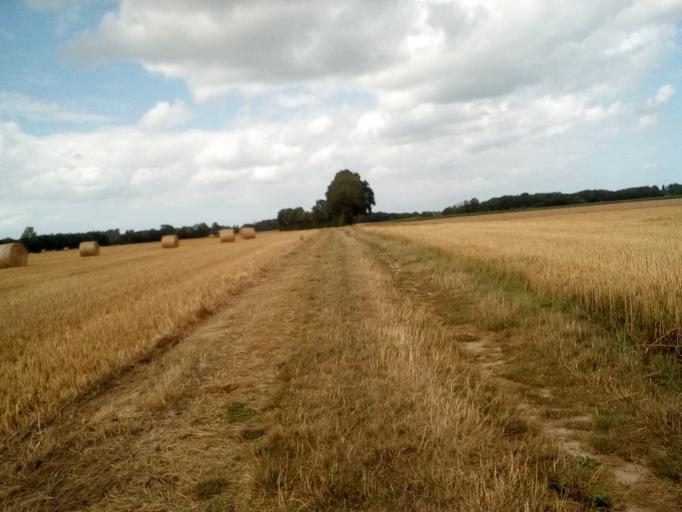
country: FR
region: Lower Normandy
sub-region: Departement du Calvados
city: Creully
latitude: 49.2979
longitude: -0.5699
